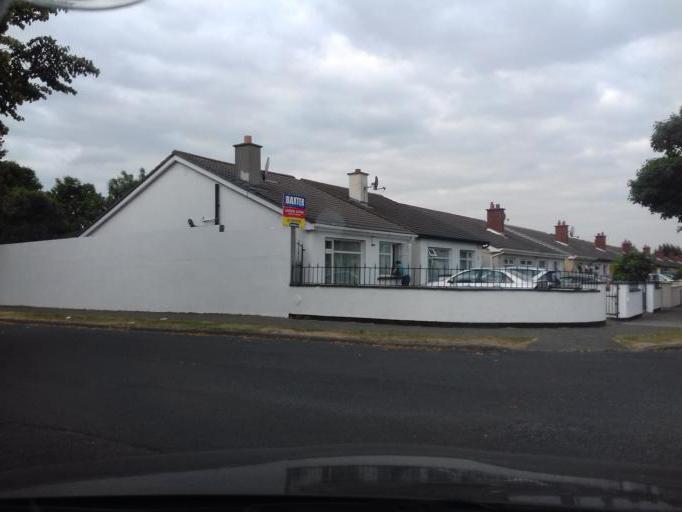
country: IE
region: Leinster
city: Hartstown
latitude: 53.4000
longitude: -6.4118
